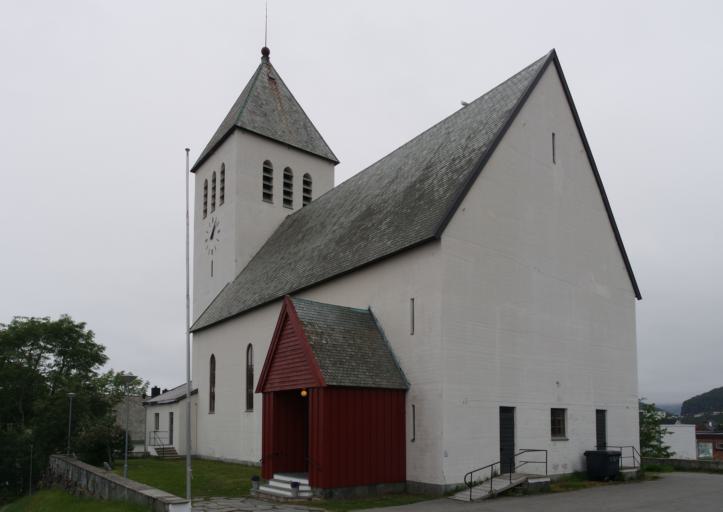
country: NO
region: Nordland
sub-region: Vagan
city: Svolvaer
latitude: 68.2335
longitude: 14.5639
